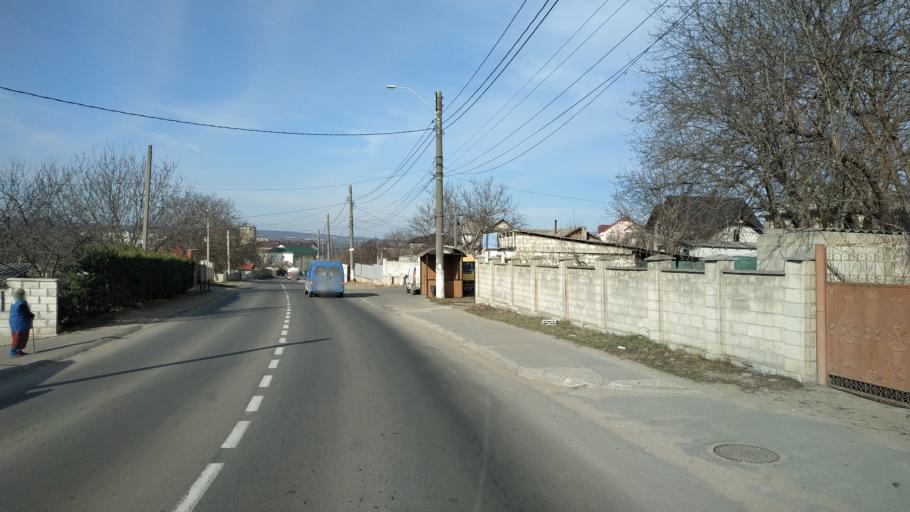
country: MD
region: Laloveni
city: Ialoveni
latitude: 46.9424
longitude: 28.7828
